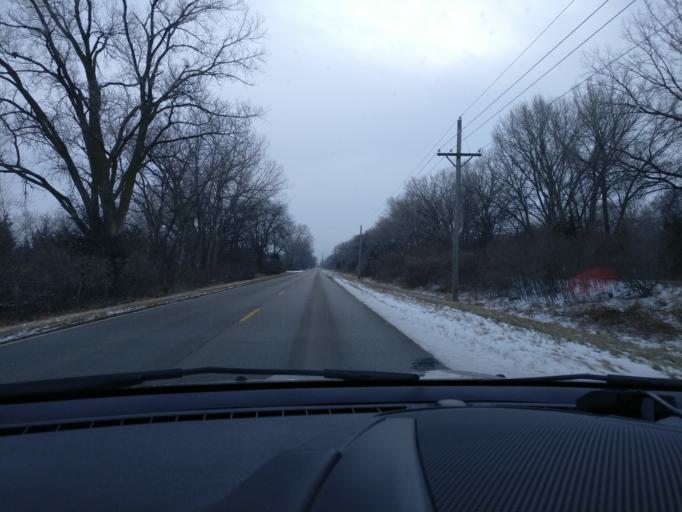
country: US
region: Nebraska
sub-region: Dodge County
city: Fremont
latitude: 41.4451
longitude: -96.5435
